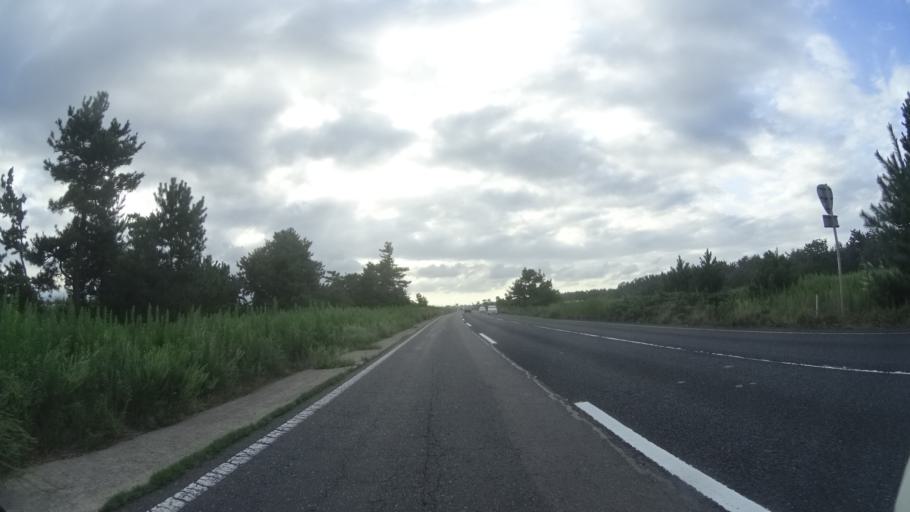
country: JP
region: Tottori
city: Kurayoshi
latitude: 35.4982
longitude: 133.7832
